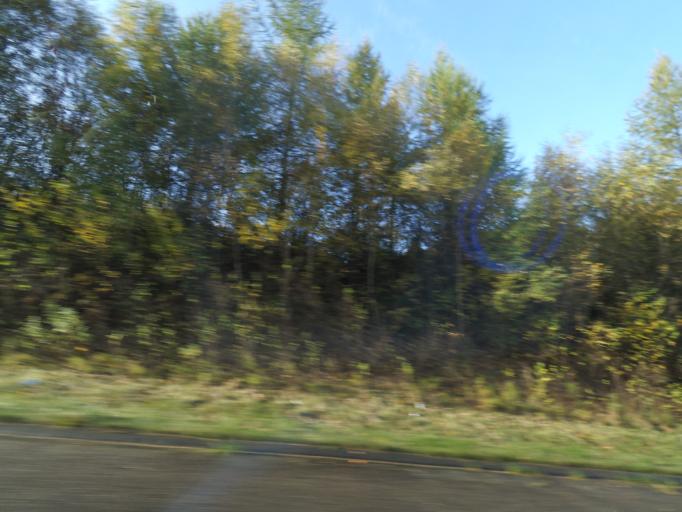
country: DK
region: South Denmark
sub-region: Fredericia Kommune
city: Taulov
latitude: 55.5533
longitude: 9.6357
